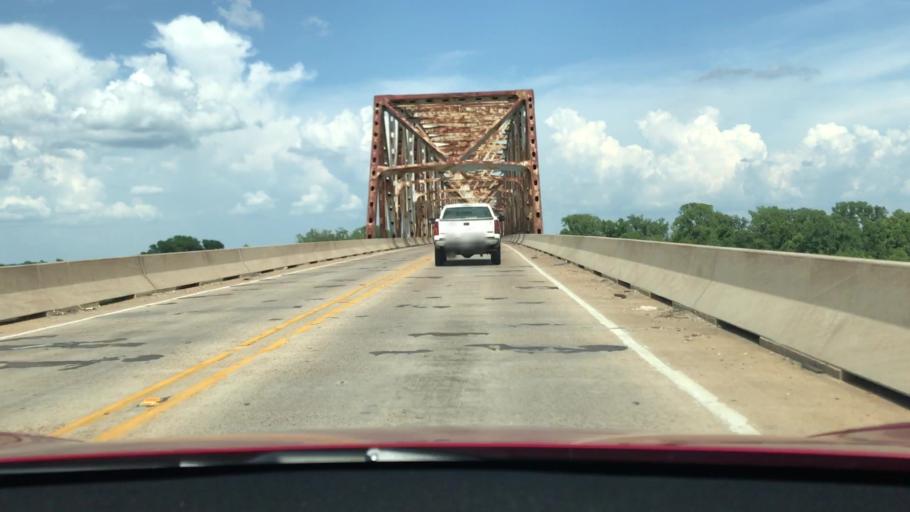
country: US
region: Louisiana
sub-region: Bossier Parish
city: Bossier City
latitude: 32.4588
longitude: -93.6809
